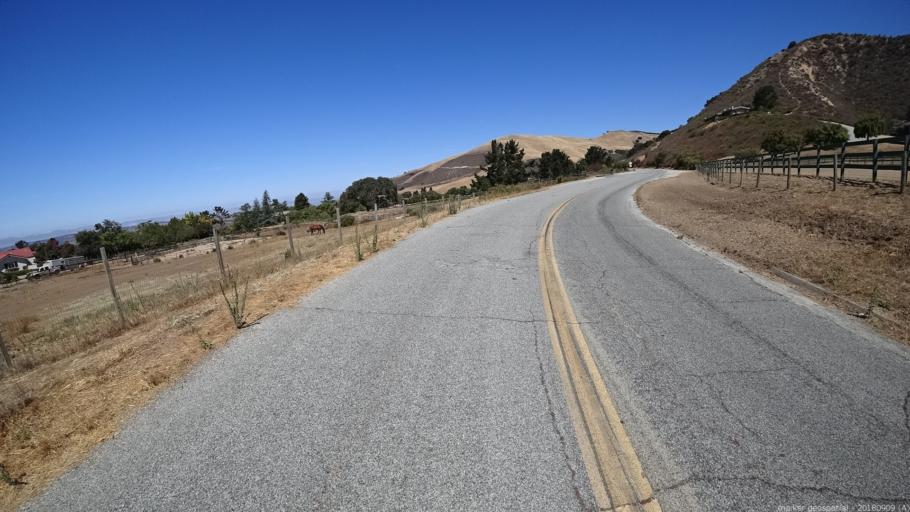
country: US
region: California
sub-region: Monterey County
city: Carmel Valley Village
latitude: 36.5433
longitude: -121.6675
